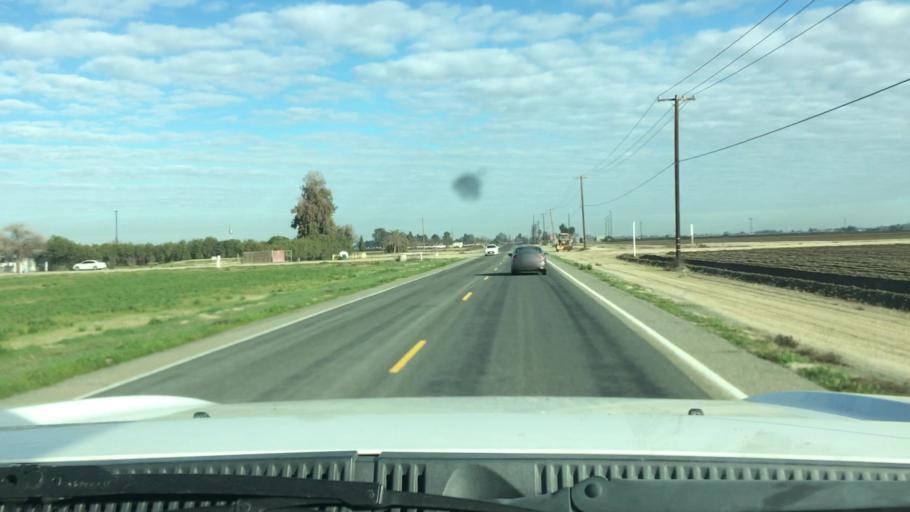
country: US
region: California
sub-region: Kings County
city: Stratford
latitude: 36.2176
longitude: -119.7803
